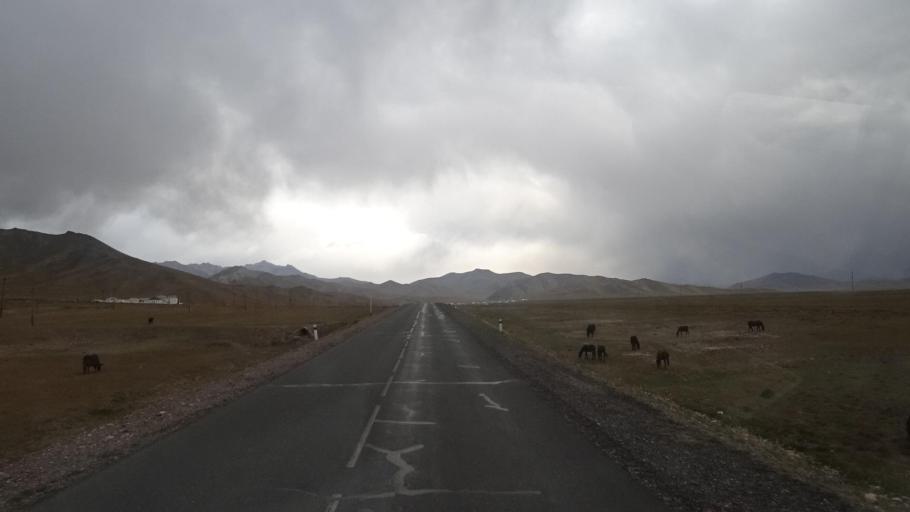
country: KG
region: Osh
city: Gul'cha
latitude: 39.7084
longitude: 73.2322
